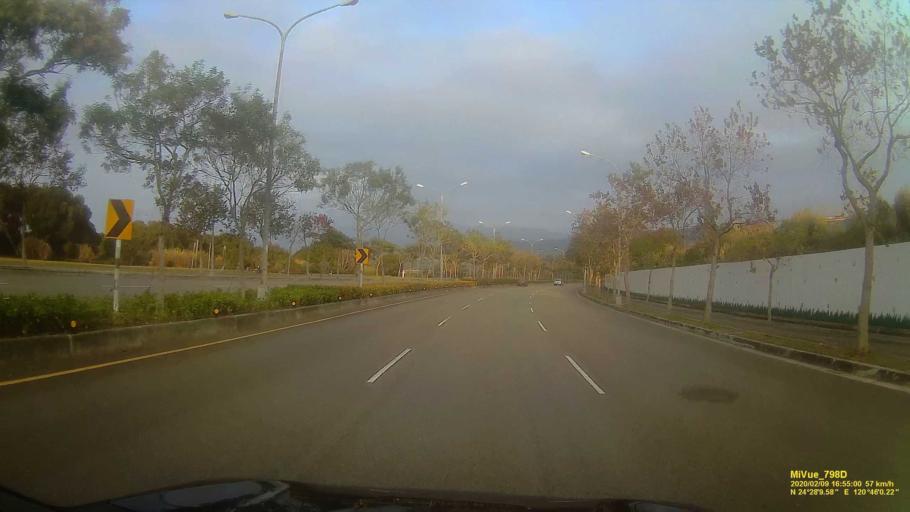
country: TW
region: Taiwan
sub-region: Miaoli
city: Miaoli
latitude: 24.4694
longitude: 120.7670
